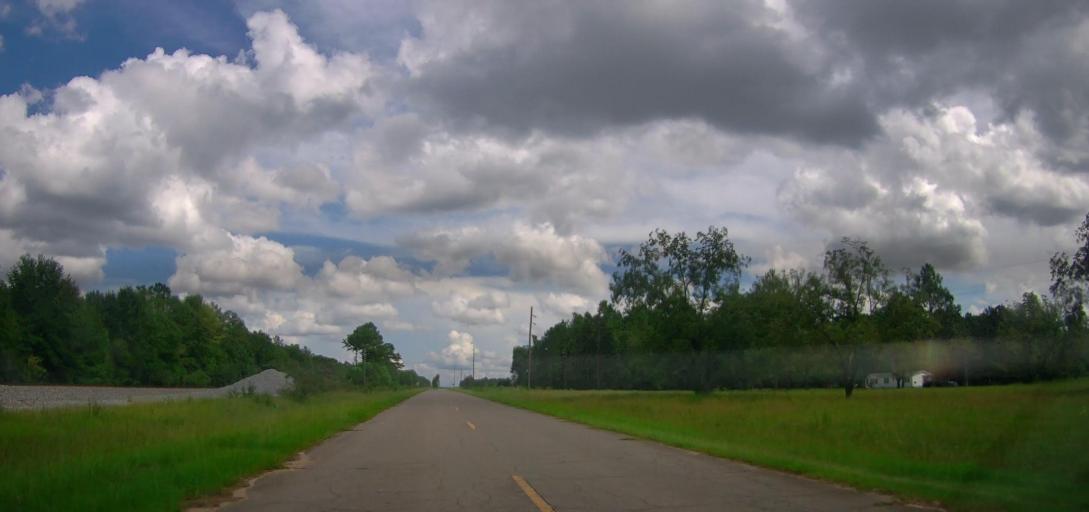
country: US
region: Georgia
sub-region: Taylor County
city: Butler
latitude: 32.5908
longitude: -84.3617
